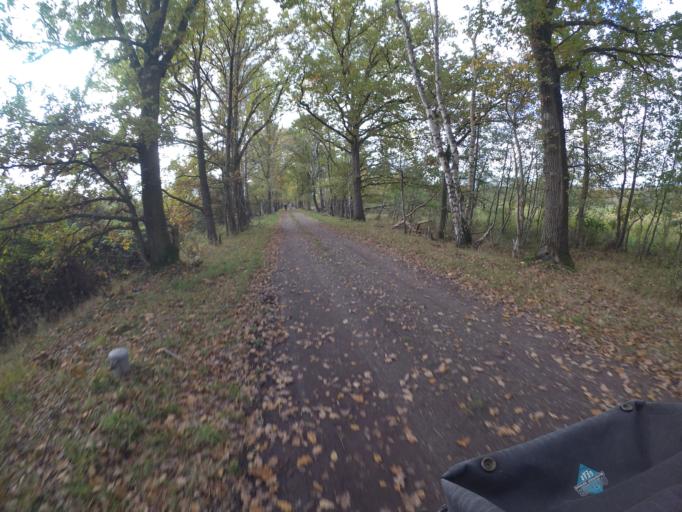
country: NL
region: North Brabant
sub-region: Gemeente Oirschot
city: Oirschot
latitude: 51.5539
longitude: 5.2799
